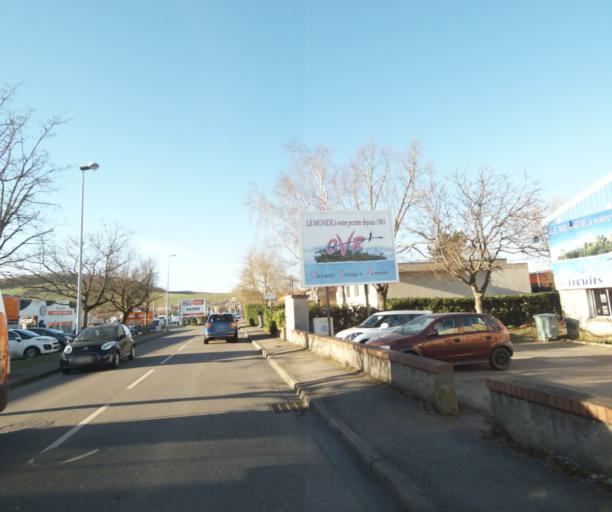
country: FR
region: Lorraine
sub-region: Departement de Meurthe-et-Moselle
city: Pulnoy
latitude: 48.7069
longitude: 6.2466
